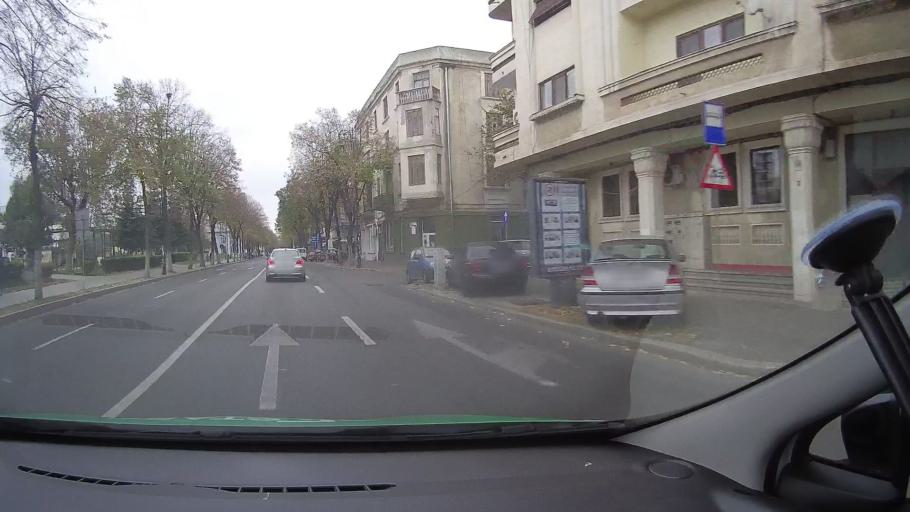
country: RO
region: Constanta
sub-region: Municipiul Constanta
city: Constanta
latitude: 44.1778
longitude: 28.6503
